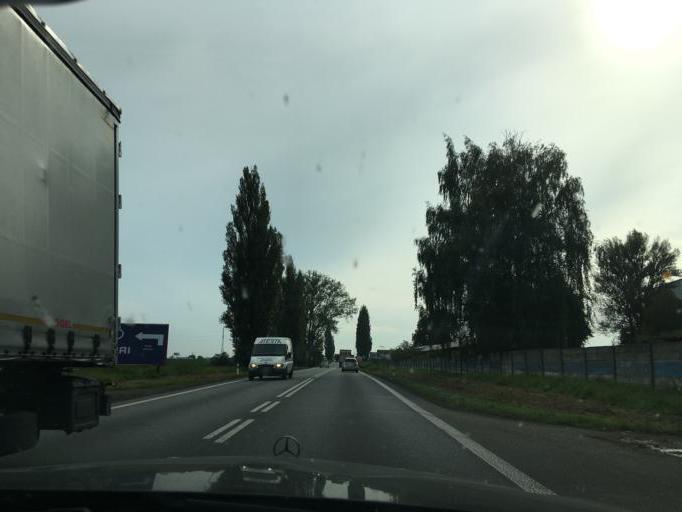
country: CZ
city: Predmerice nad Labem
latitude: 50.2400
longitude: 15.7958
